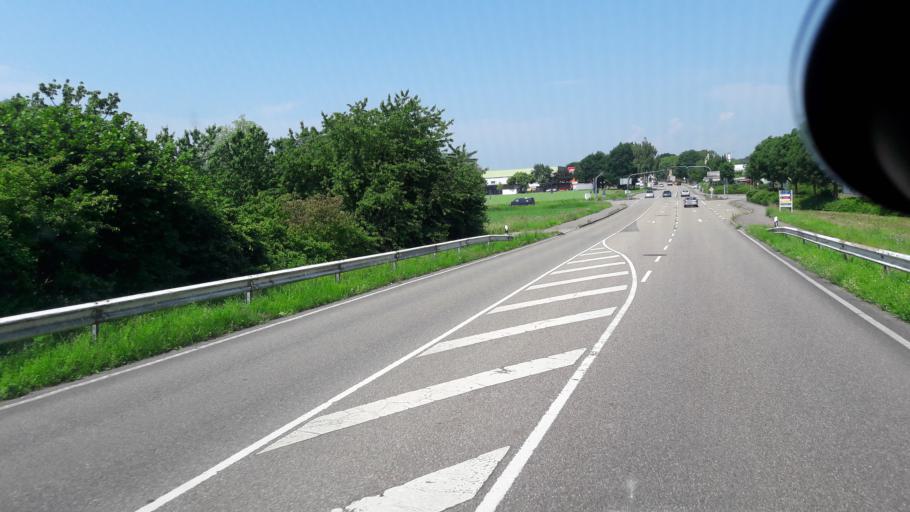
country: DE
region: Baden-Wuerttemberg
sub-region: Karlsruhe Region
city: Rastatt
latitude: 48.8583
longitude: 8.2402
